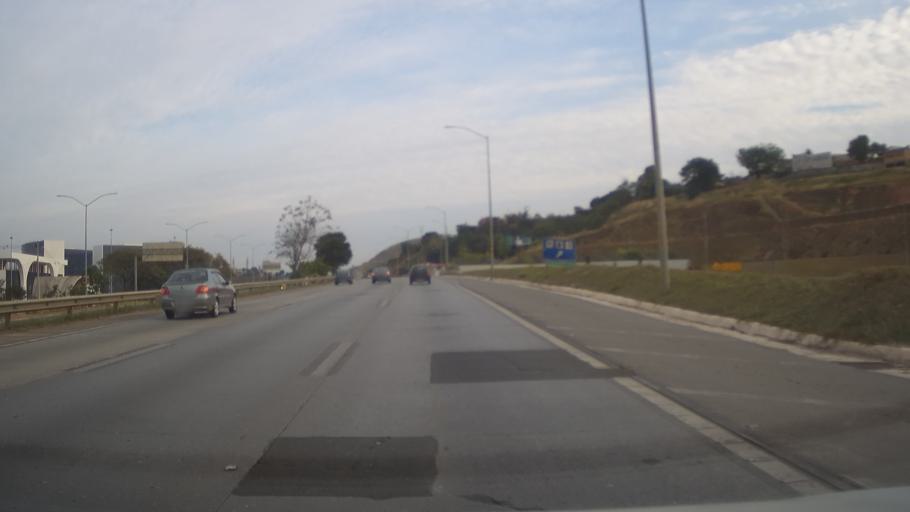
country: BR
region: Minas Gerais
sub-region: Santa Luzia
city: Santa Luzia
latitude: -19.7917
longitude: -43.9491
